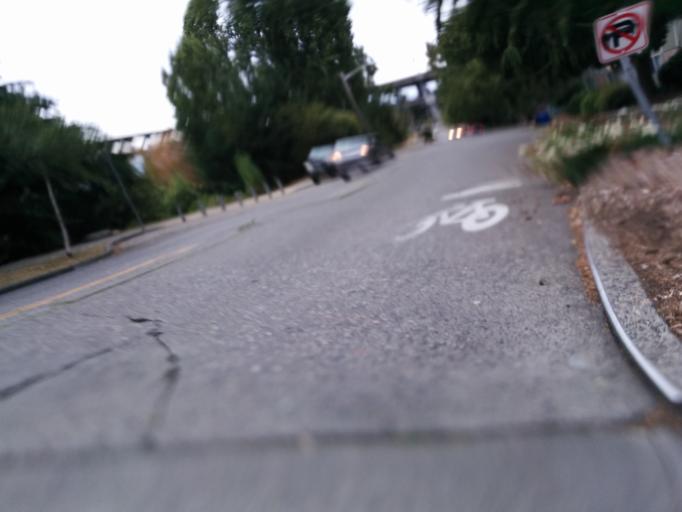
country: US
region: Washington
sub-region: King County
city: Seattle
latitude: 47.6558
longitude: -122.3189
